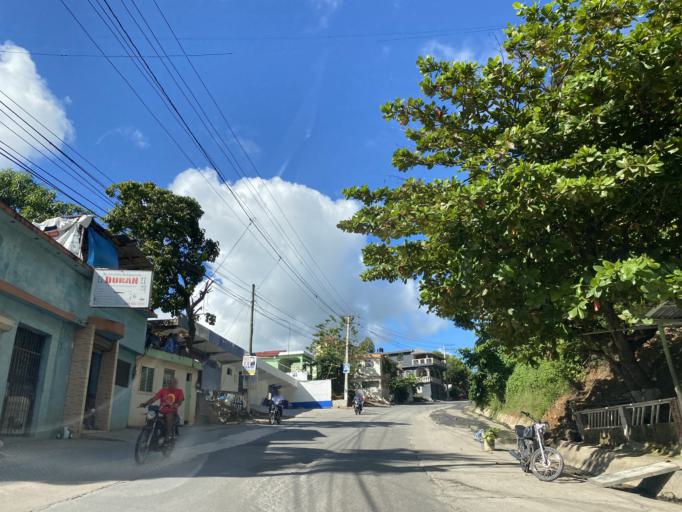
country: DO
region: Samana
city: Samana
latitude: 19.2085
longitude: -69.3547
